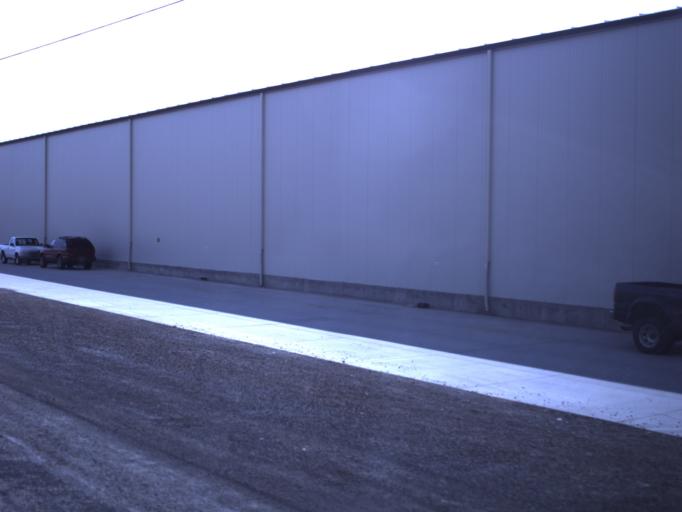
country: US
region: Utah
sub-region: Box Elder County
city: Garland
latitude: 41.7729
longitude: -112.0960
